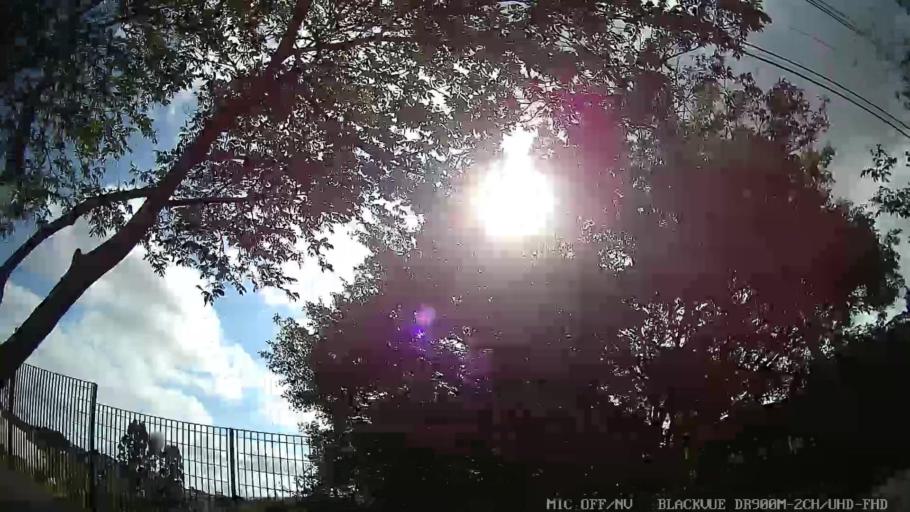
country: BR
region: Sao Paulo
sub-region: Guarulhos
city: Guarulhos
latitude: -23.5242
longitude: -46.4751
